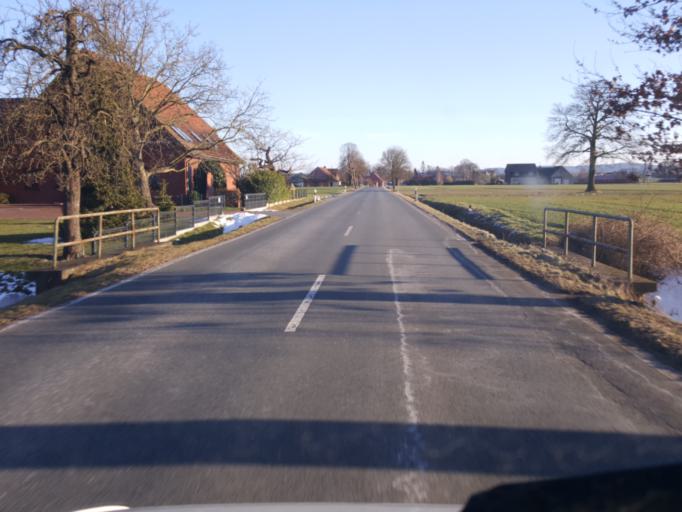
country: DE
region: North Rhine-Westphalia
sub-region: Regierungsbezirk Detmold
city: Hille
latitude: 52.3613
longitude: 8.7290
